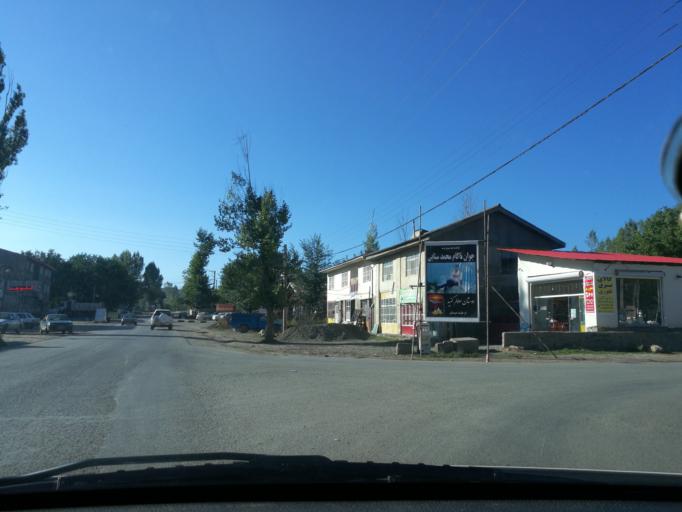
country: IR
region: Mazandaran
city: `Abbasabad
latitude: 36.5383
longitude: 51.1802
